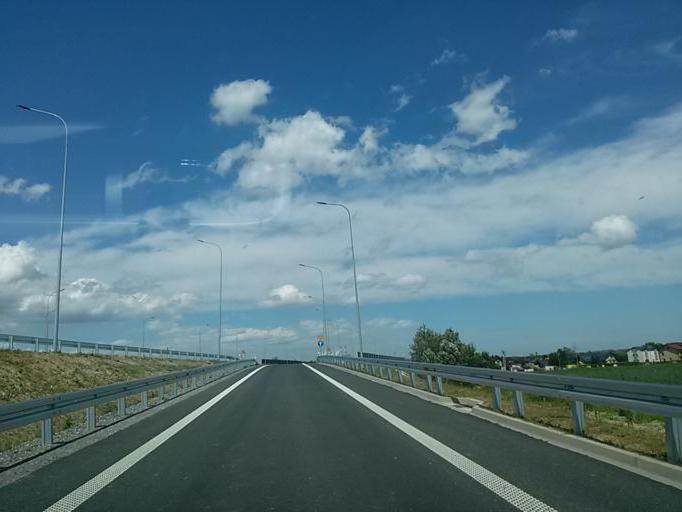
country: PL
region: Lesser Poland Voivodeship
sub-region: Powiat wielicki
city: Kokotow
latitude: 50.0386
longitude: 20.0652
